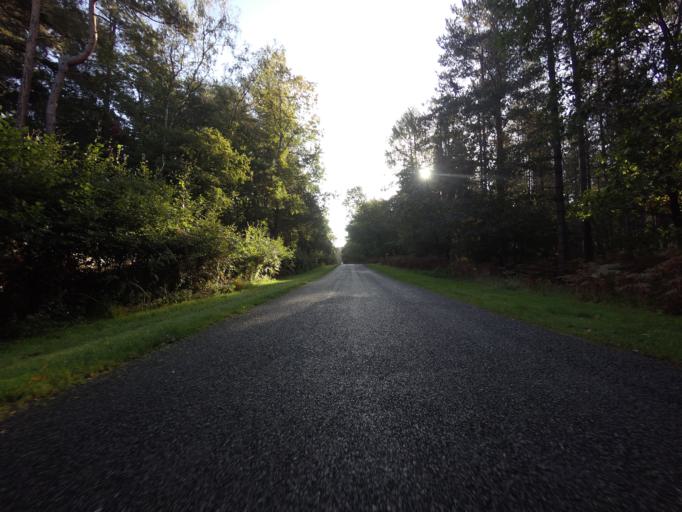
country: GB
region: England
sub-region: Norfolk
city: Dersingham
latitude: 52.8159
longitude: 0.5033
